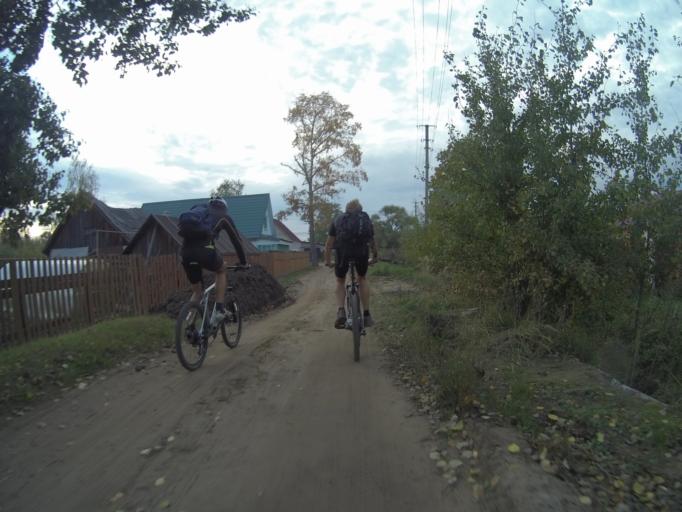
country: RU
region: Vladimir
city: Sobinka
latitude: 55.9853
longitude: 40.0102
